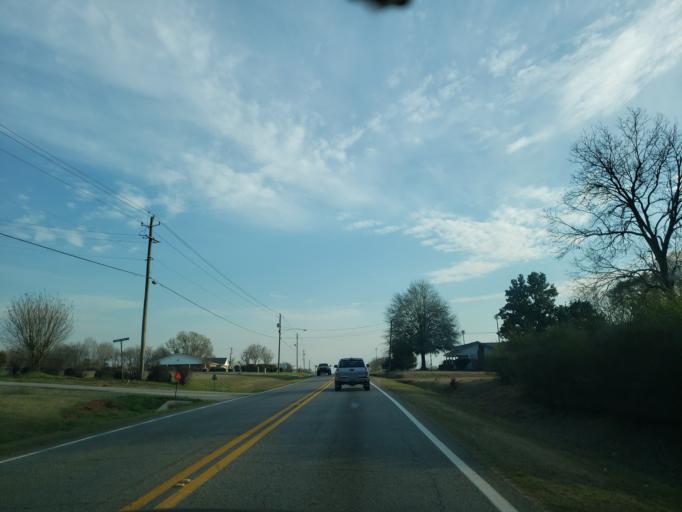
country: US
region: Alabama
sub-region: Hale County
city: Moundville
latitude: 32.9919
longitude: -87.6244
